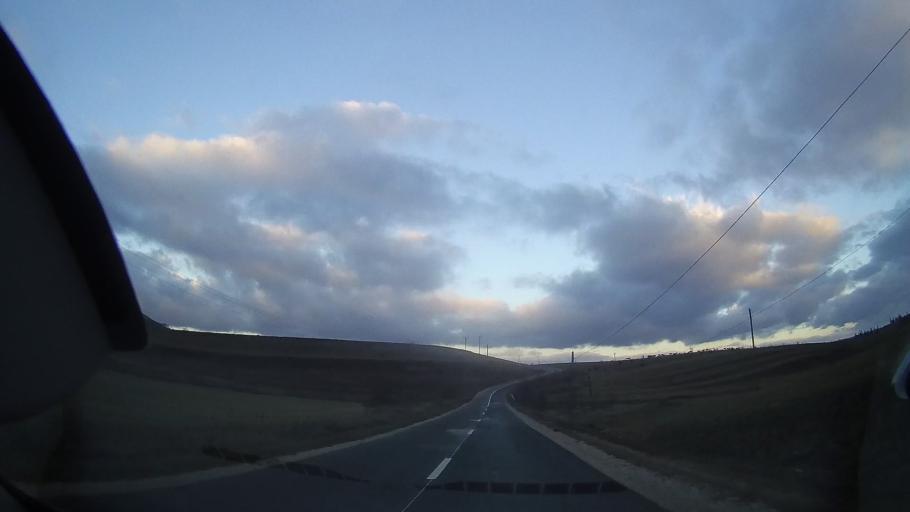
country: RO
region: Cluj
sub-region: Comuna Manastireni
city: Manastireni
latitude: 46.7893
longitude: 23.0979
